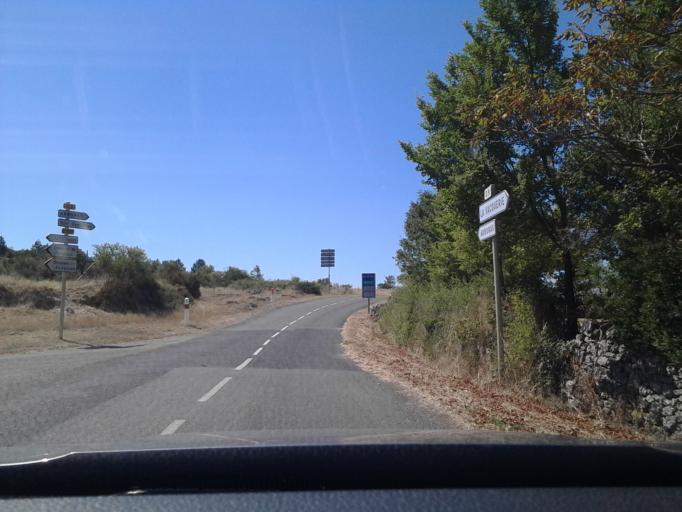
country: FR
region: Languedoc-Roussillon
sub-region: Departement de l'Herault
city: Montpeyroux
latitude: 43.7751
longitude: 3.4681
